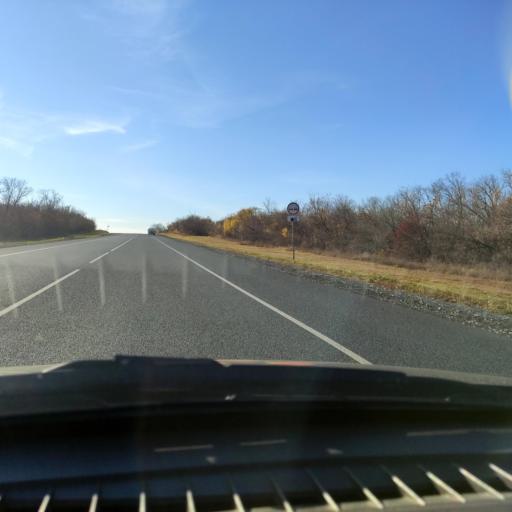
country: RU
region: Samara
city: Mezhdurechensk
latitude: 53.2547
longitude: 49.0456
